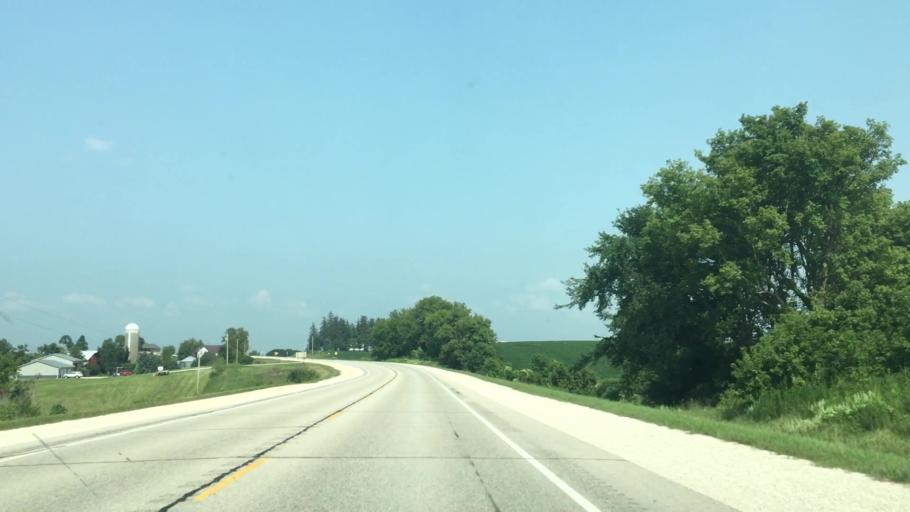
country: US
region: Iowa
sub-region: Winneshiek County
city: Decorah
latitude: 43.2770
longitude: -91.8159
